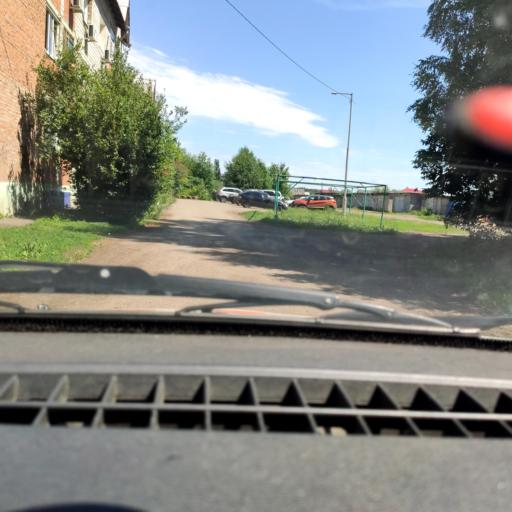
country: RU
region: Bashkortostan
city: Ufa
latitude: 54.5687
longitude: 55.8999
